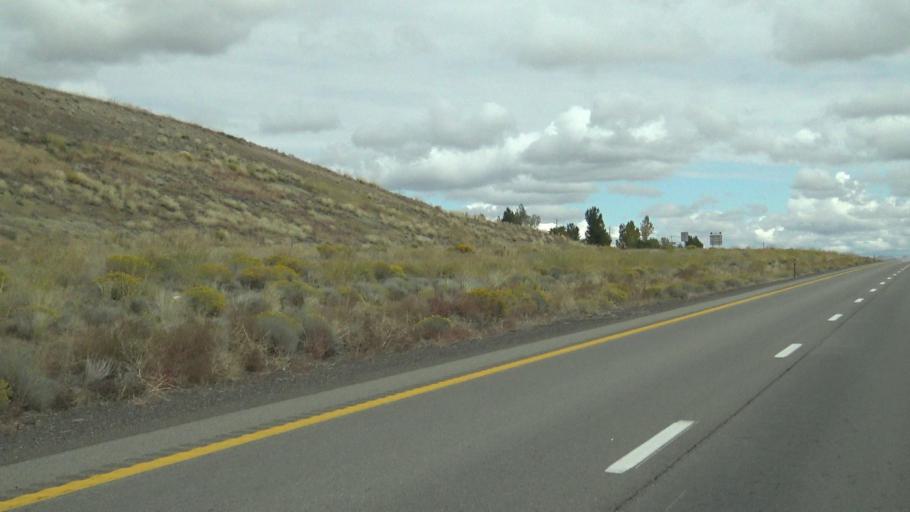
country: US
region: Nevada
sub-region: Elko County
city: Elko
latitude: 40.9271
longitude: -115.6754
